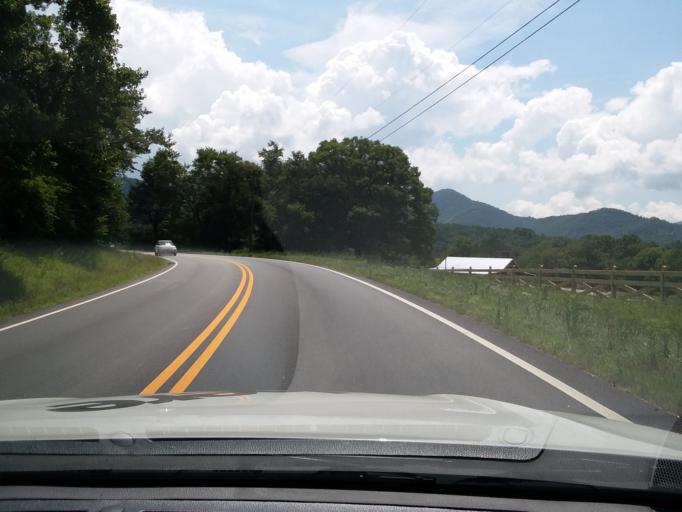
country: US
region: Georgia
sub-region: Rabun County
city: Mountain City
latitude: 34.9844
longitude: -83.3779
